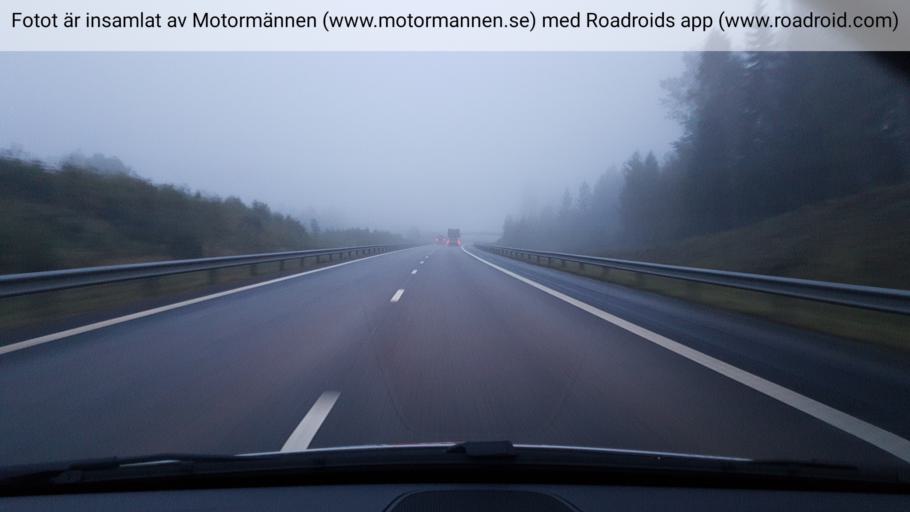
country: SE
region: Gaevleborg
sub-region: Gavle Kommun
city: Gavle
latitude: 60.5555
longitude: 17.2533
